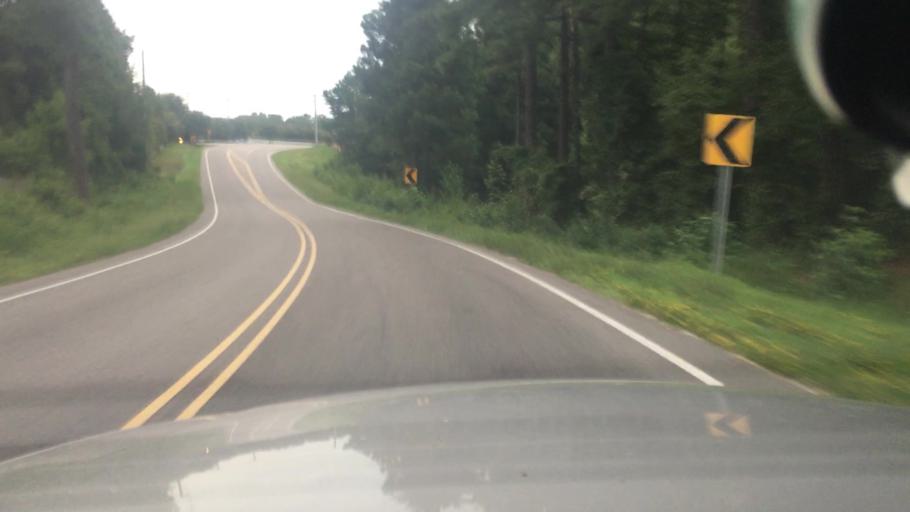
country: US
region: North Carolina
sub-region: Hoke County
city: Rockfish
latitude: 34.9985
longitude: -79.0237
